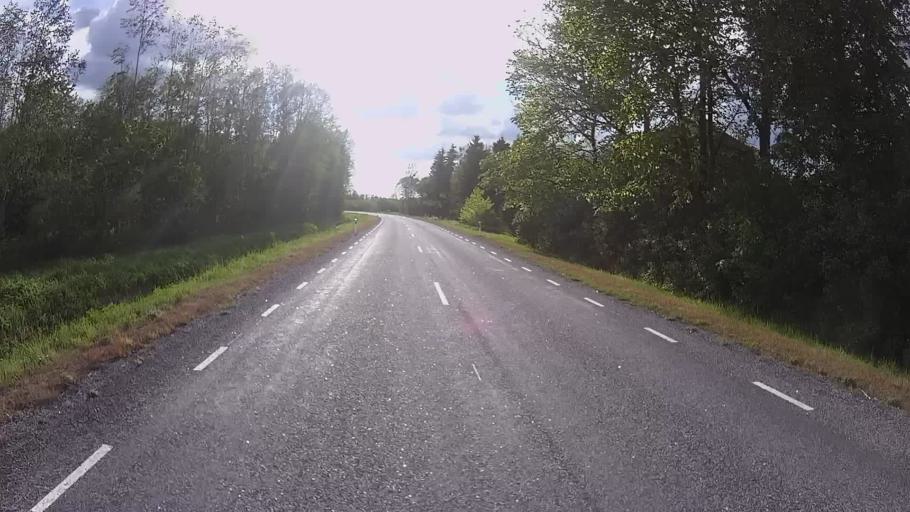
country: EE
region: Jogevamaa
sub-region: Mustvee linn
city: Mustvee
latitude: 59.0263
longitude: 26.9916
